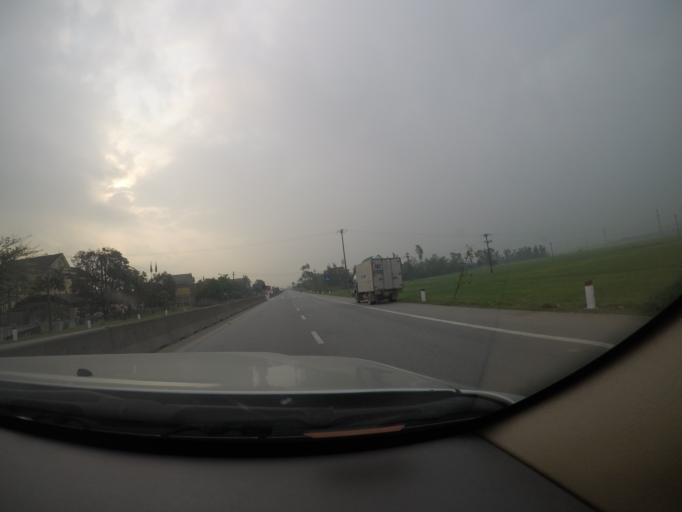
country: VN
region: Ha Tinh
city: Cam Xuyen
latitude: 18.2388
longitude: 106.0181
